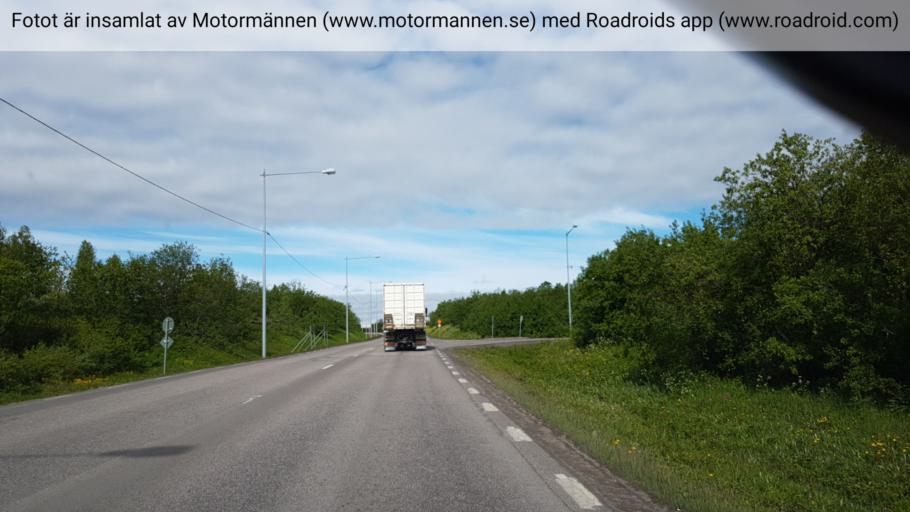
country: SE
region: Norrbotten
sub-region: Kiruna Kommun
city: Kiruna
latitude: 67.8437
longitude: 20.2728
